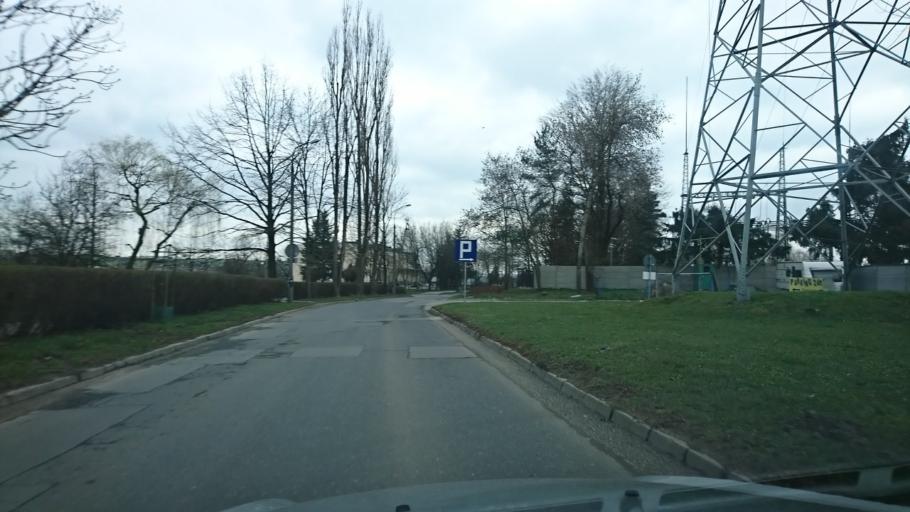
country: PL
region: Lesser Poland Voivodeship
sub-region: Powiat wielicki
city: Czarnochowice
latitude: 50.0132
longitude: 20.0237
